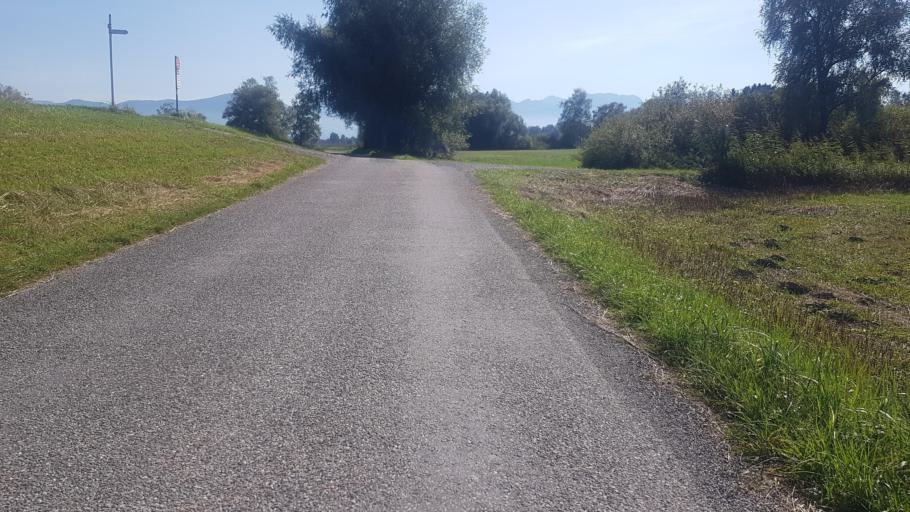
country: AT
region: Vorarlberg
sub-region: Politischer Bezirk Bregenz
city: Fussach
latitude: 47.4874
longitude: 9.6464
